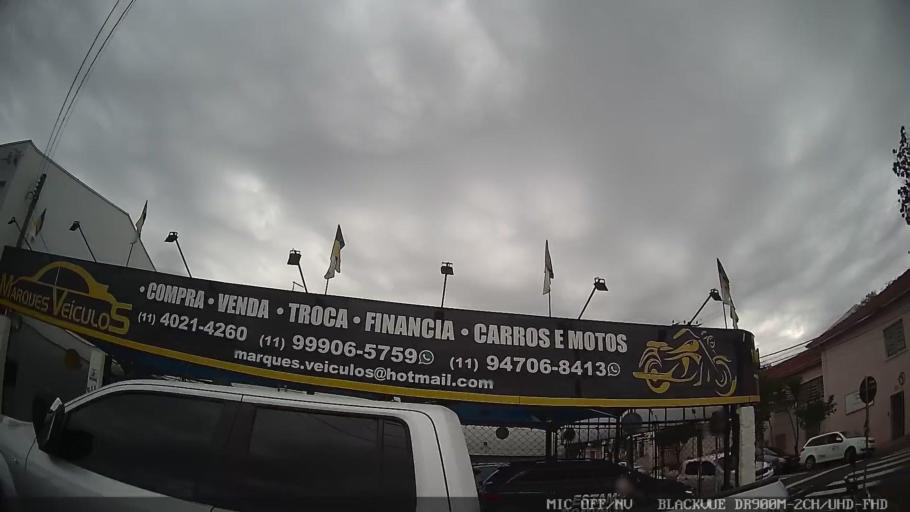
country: BR
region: Sao Paulo
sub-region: Salto
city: Salto
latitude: -23.2056
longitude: -47.2896
